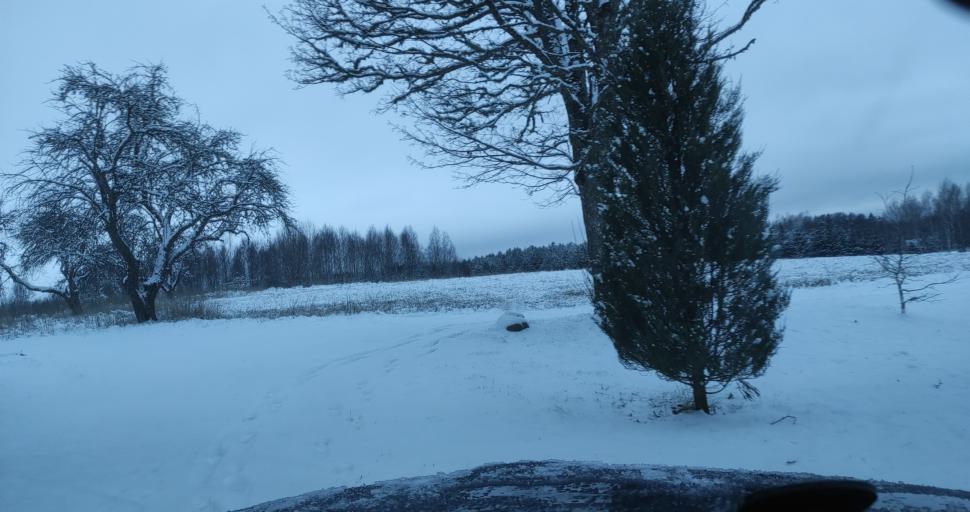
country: LV
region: Alsunga
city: Alsunga
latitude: 56.9564
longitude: 21.6228
